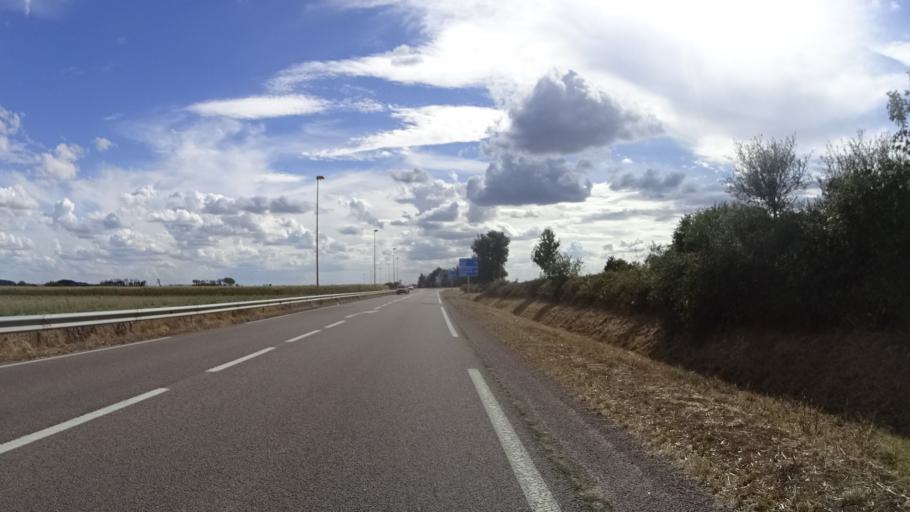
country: FR
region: Bourgogne
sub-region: Departement de la Cote-d'Or
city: Seurre
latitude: 47.0290
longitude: 5.1724
